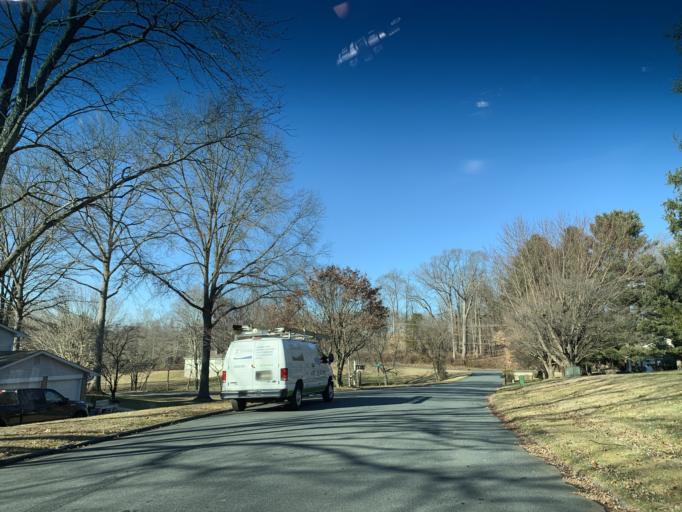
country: US
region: Maryland
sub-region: Harford County
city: Riverside
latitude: 39.5337
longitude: -76.2541
